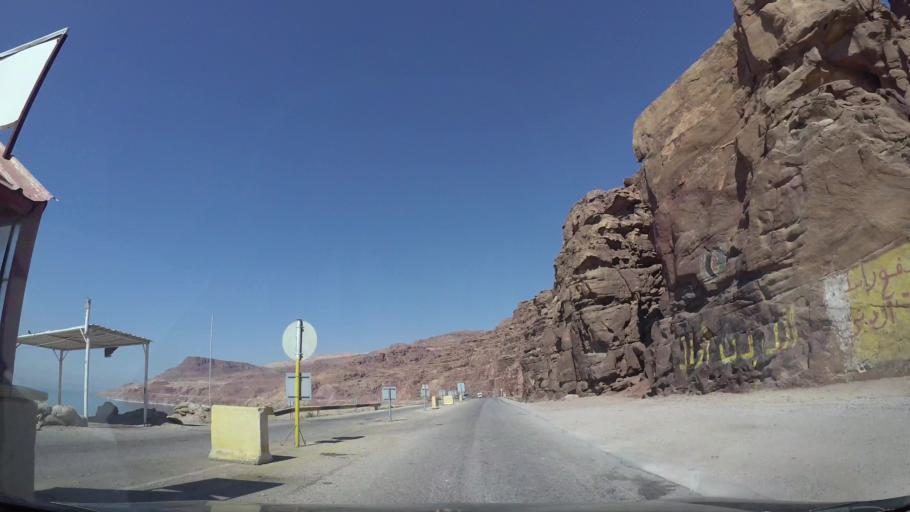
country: JO
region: Karak
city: Al Qasr
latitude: 31.4696
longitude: 35.5734
